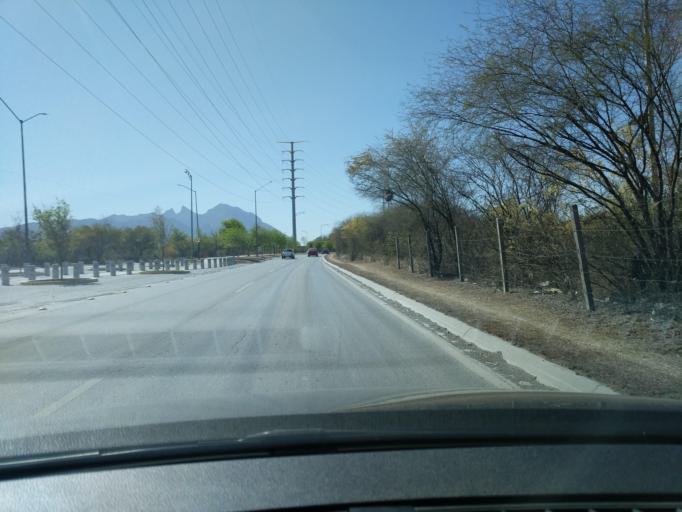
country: MX
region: Nuevo Leon
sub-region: Juarez
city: Hector Caballero
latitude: 25.6196
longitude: -100.1094
